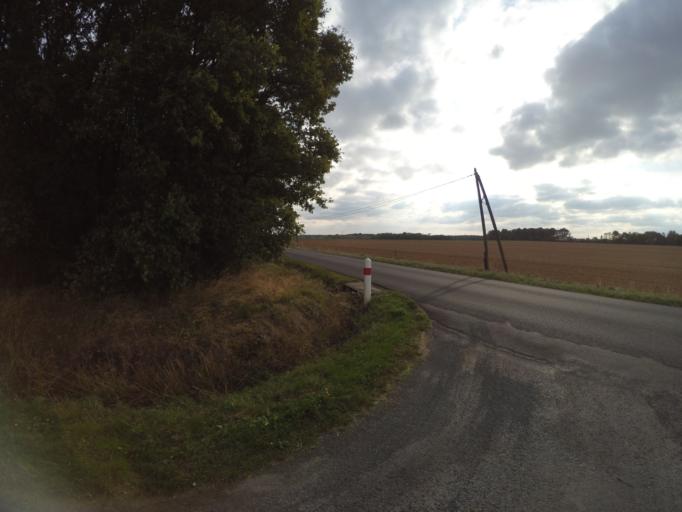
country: FR
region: Centre
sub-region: Departement d'Indre-et-Loire
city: Nazelles-Negron
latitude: 47.4813
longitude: 0.9503
